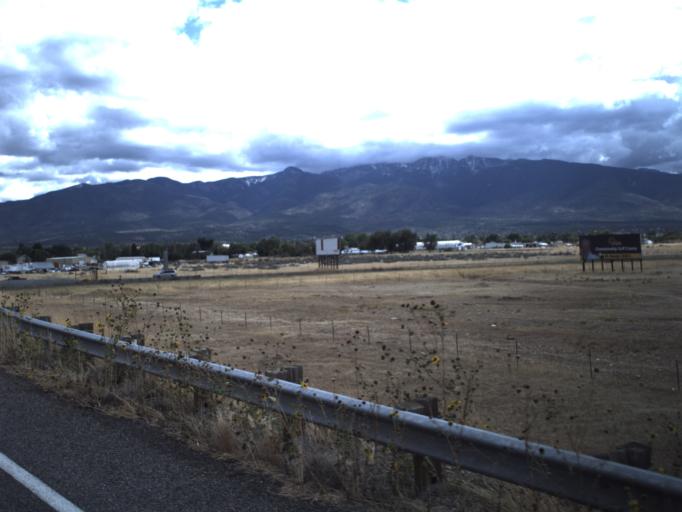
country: US
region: Utah
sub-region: Millard County
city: Fillmore
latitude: 38.9790
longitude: -112.3402
